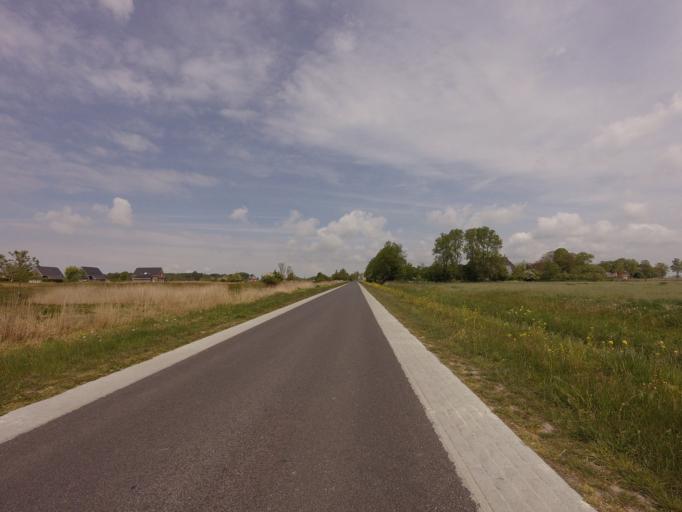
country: NL
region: Friesland
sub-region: Sudwest Fryslan
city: Bolsward
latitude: 53.0969
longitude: 5.4784
